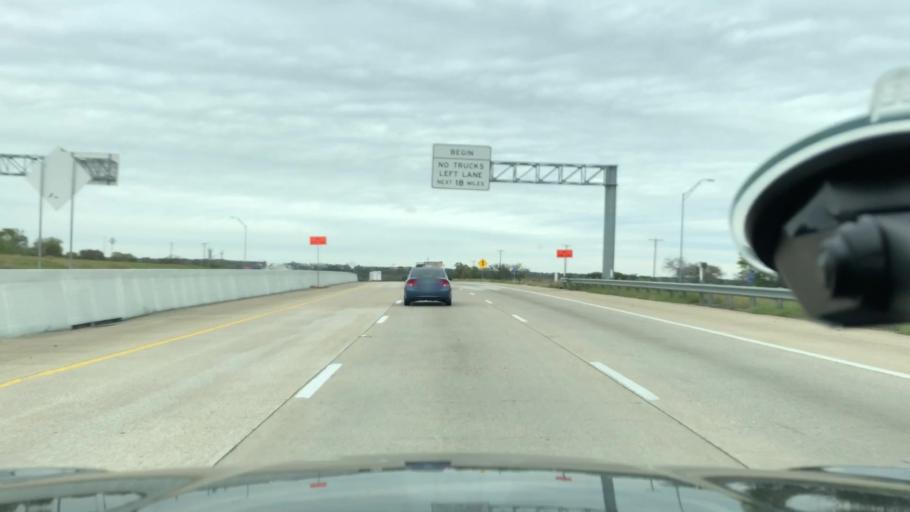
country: US
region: Texas
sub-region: Ellis County
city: Red Oak
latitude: 32.4988
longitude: -96.8224
